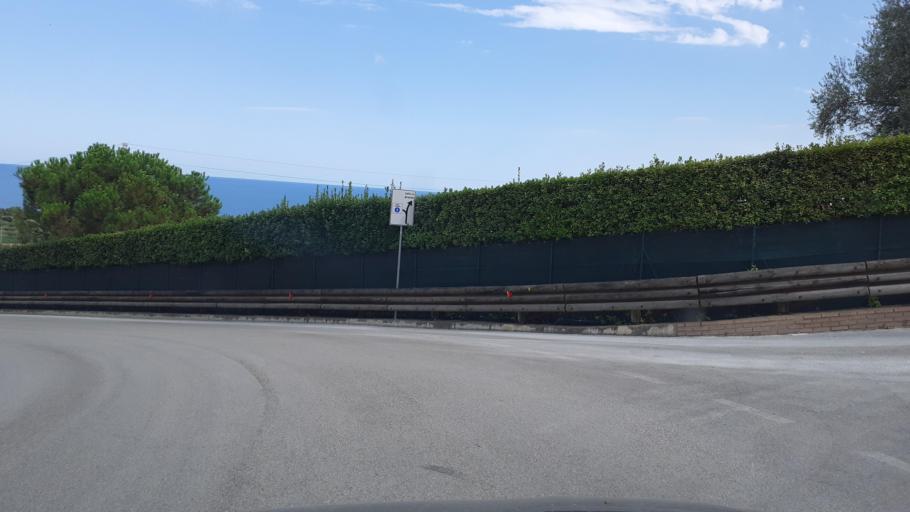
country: IT
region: Abruzzo
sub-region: Provincia di Chieti
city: Fossacesia
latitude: 42.2526
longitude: 14.4976
